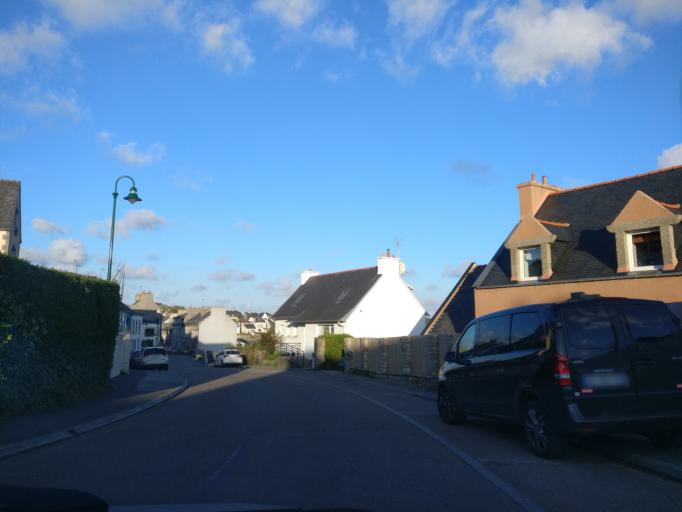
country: FR
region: Brittany
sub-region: Departement du Finistere
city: Lampaul-Plouarzel
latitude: 48.4732
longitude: -4.7546
